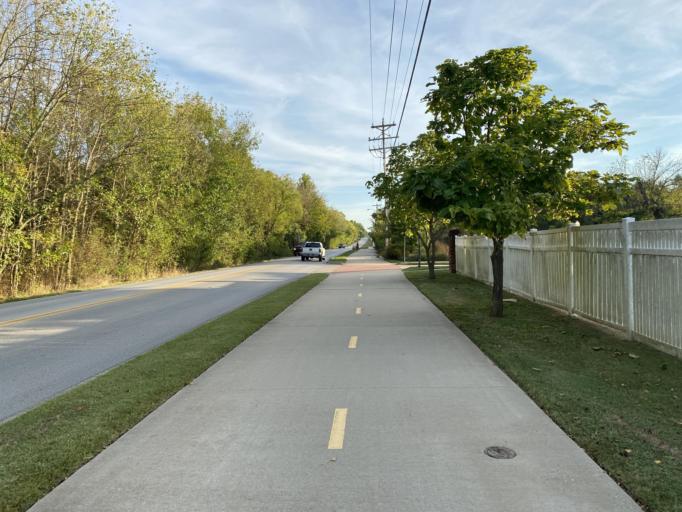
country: US
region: Arkansas
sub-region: Washington County
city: Johnson
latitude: 36.1014
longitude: -94.2080
